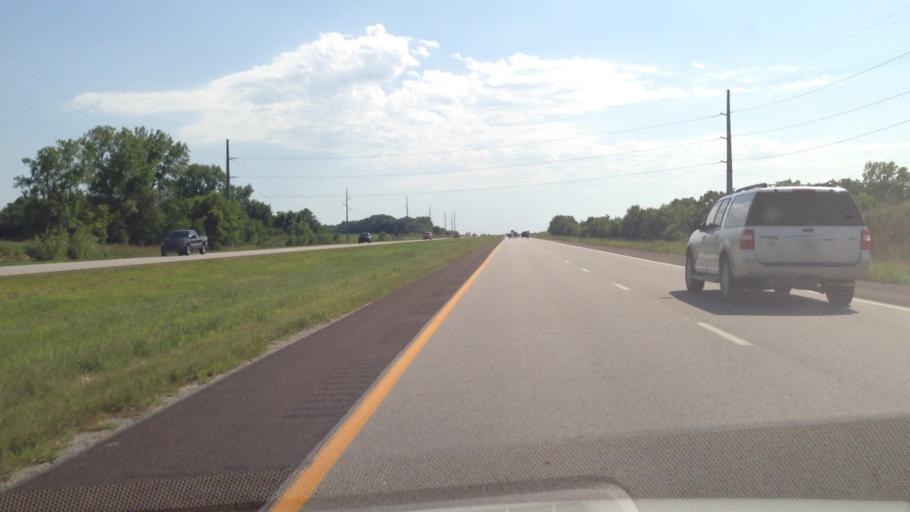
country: US
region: Kansas
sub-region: Miami County
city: Louisburg
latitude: 38.6478
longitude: -94.6879
